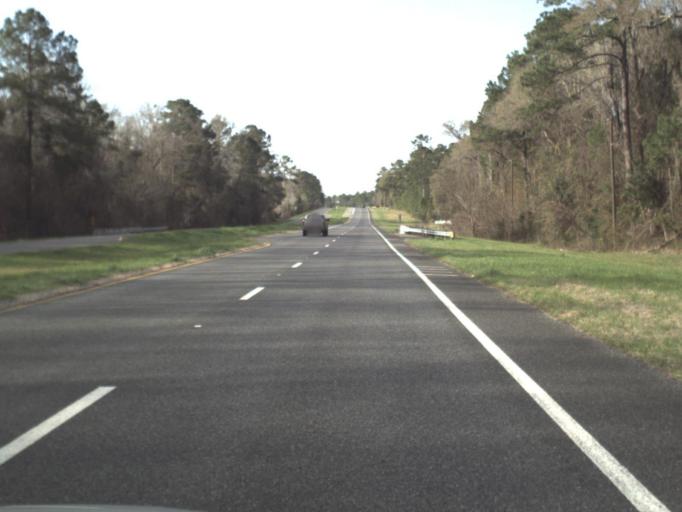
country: US
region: Florida
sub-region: Jefferson County
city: Monticello
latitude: 30.6533
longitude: -83.8765
